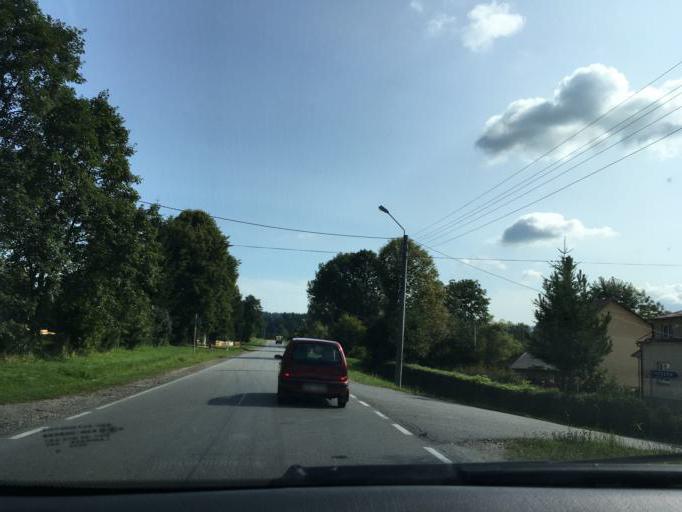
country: PL
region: Subcarpathian Voivodeship
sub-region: Powiat bieszczadzki
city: Ustrzyki Dolne
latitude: 49.3958
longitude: 22.6447
